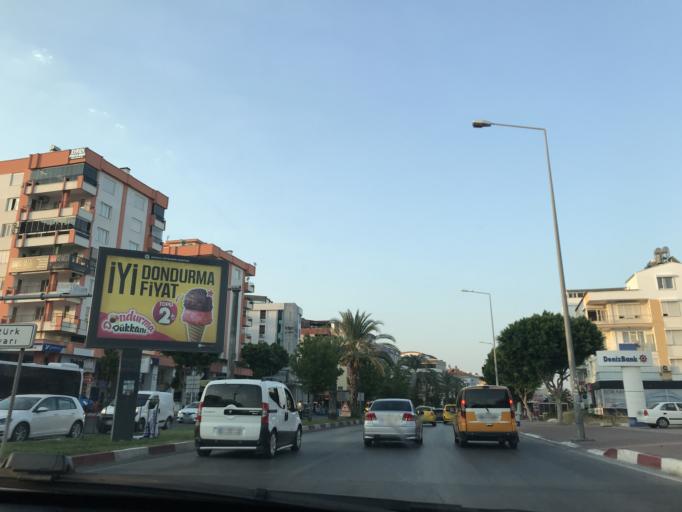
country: TR
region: Antalya
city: Antalya
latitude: 36.8747
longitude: 30.6429
